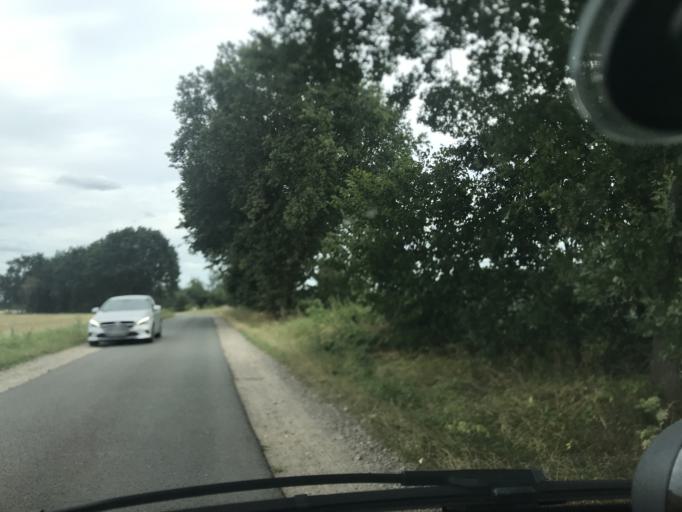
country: DE
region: Lower Saxony
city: Moisburg
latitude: 53.4020
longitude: 9.7117
